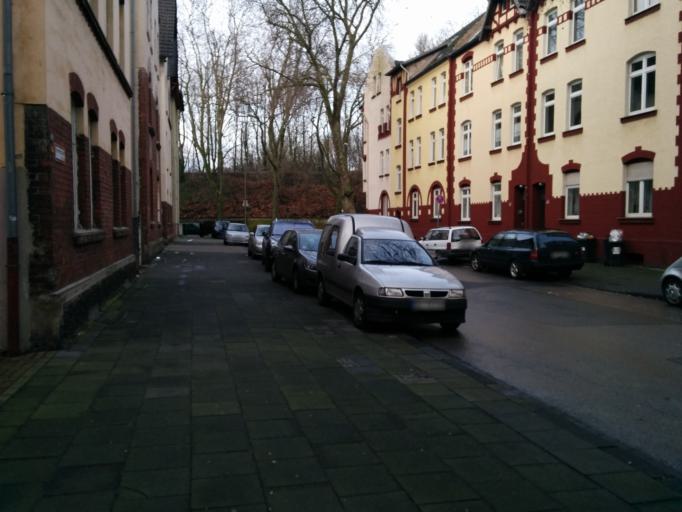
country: DE
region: North Rhine-Westphalia
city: Meiderich
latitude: 51.4757
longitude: 6.7843
